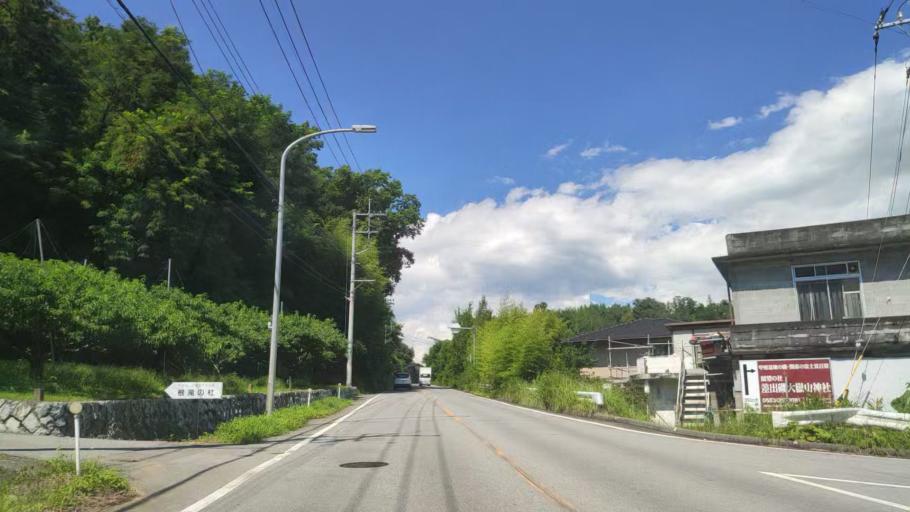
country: JP
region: Yamanashi
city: Enzan
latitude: 35.6952
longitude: 138.6817
